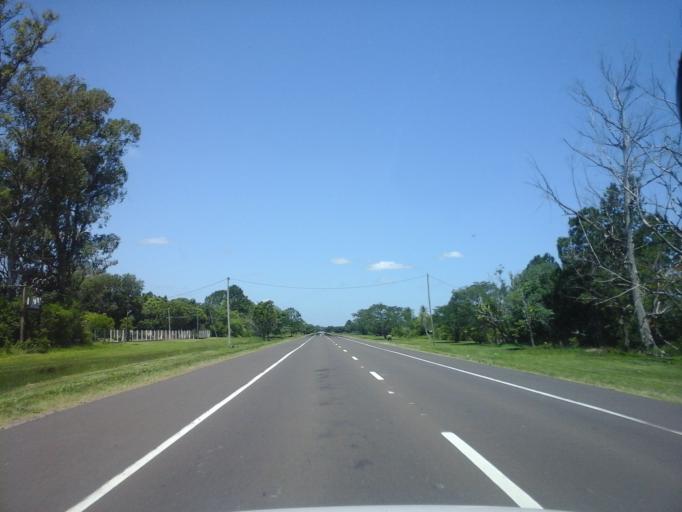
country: AR
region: Corrientes
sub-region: Departamento de San Cosme
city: San Cosme
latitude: -27.3665
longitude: -58.4309
